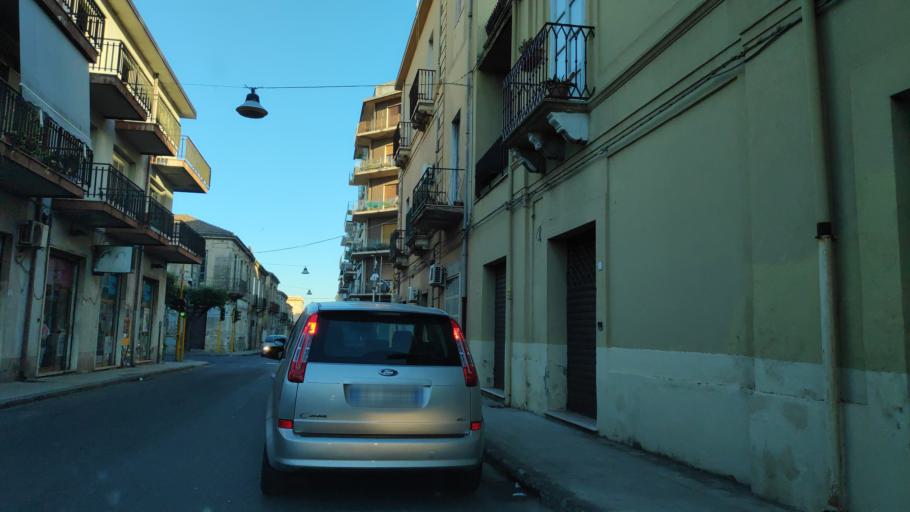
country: IT
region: Calabria
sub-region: Provincia di Reggio Calabria
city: Locri
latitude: 38.2348
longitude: 16.2619
